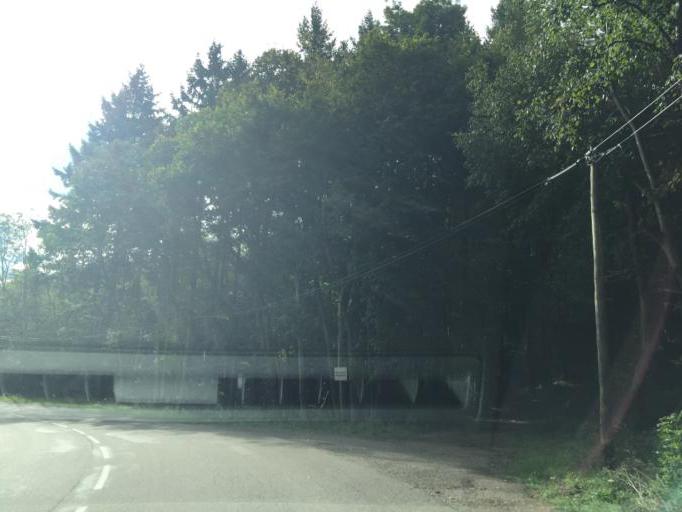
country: FR
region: Rhone-Alpes
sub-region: Departement de la Loire
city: Saint-Paul-en-Jarez
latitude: 45.4540
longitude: 4.5953
